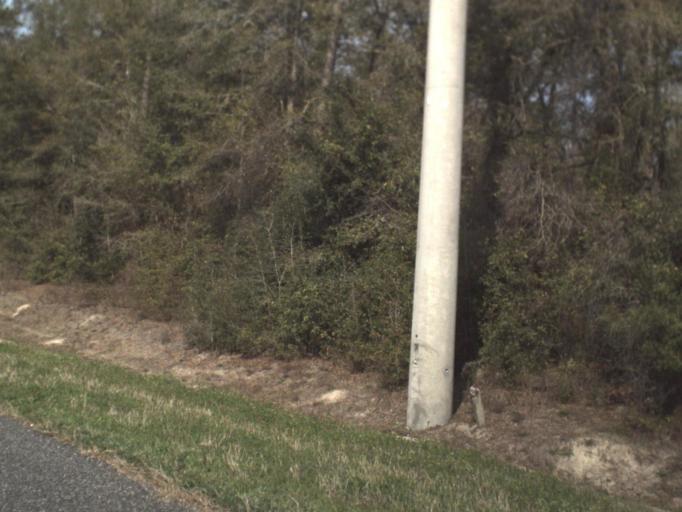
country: US
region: Florida
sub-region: Leon County
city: Woodville
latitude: 30.4195
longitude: -84.0944
